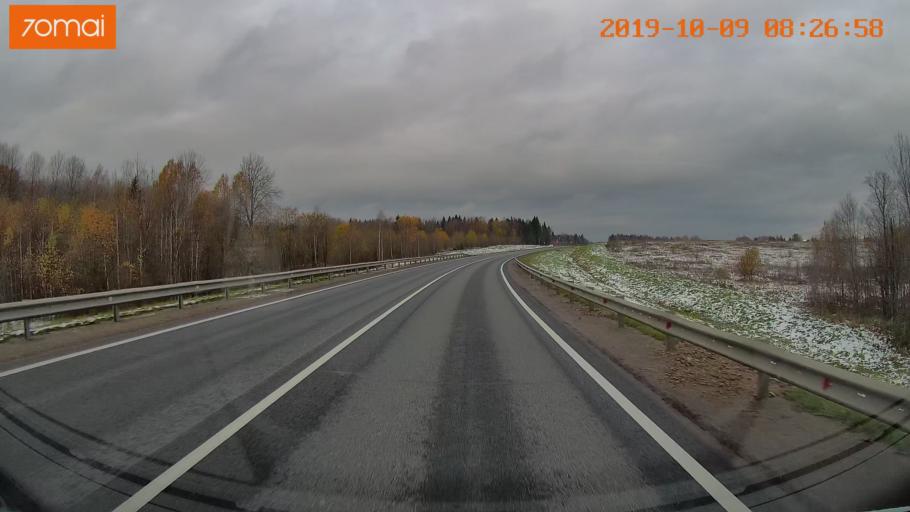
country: RU
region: Vologda
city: Gryazovets
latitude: 58.7983
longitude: 40.2570
